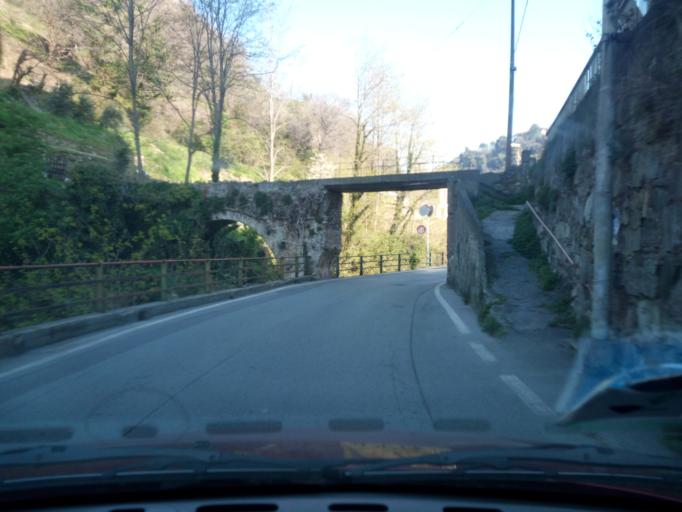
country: IT
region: Liguria
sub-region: Provincia di Genova
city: Mele
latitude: 44.4330
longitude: 8.7779
